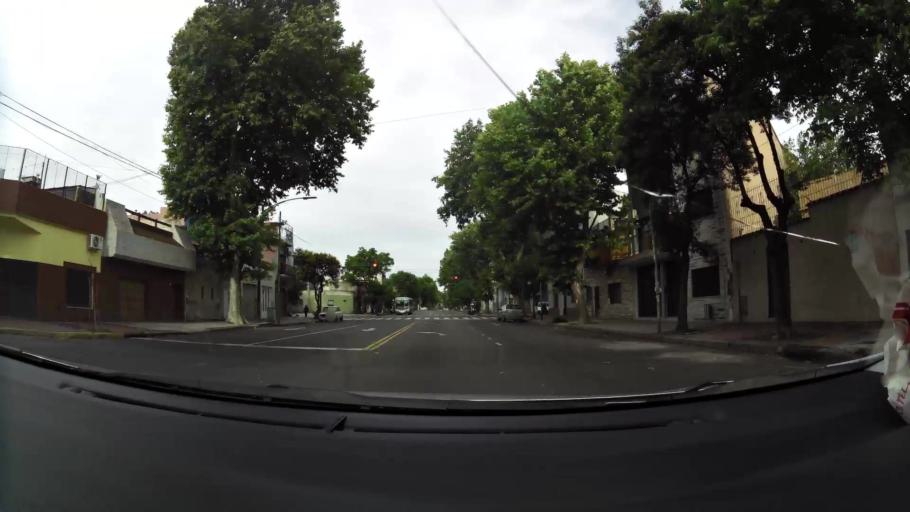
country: AR
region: Buenos Aires F.D.
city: Villa Lugano
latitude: -34.6451
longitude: -58.4311
